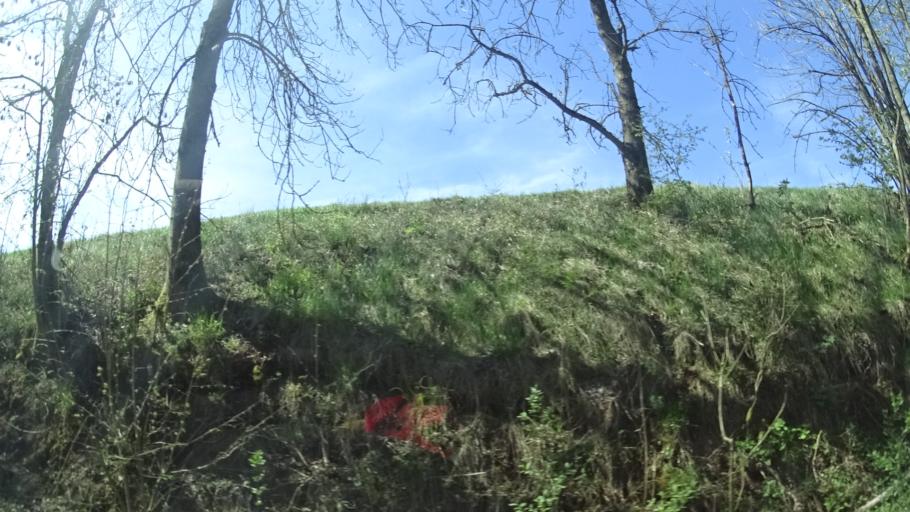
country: DE
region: Bavaria
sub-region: Upper Franconia
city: Weitramsdorf
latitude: 50.2889
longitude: 10.7879
